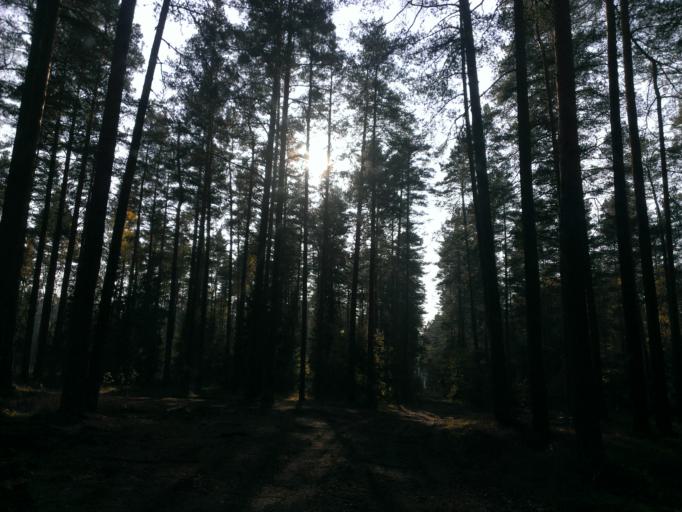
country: LV
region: Garkalne
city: Garkalne
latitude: 57.0174
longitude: 24.4668
